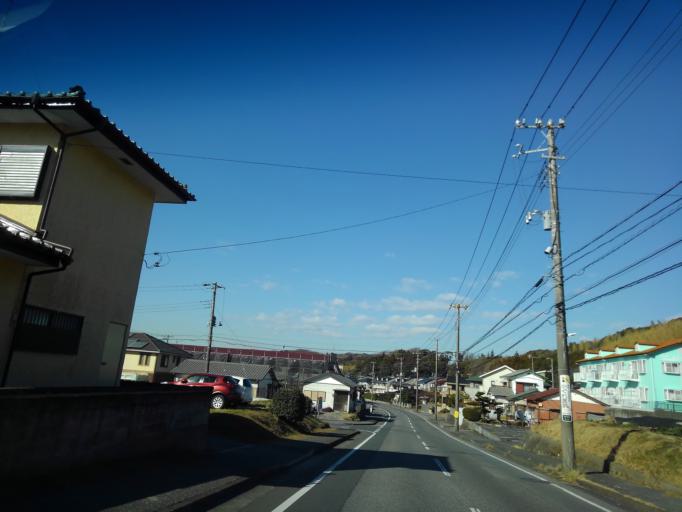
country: JP
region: Chiba
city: Kimitsu
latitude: 35.3339
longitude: 139.9213
